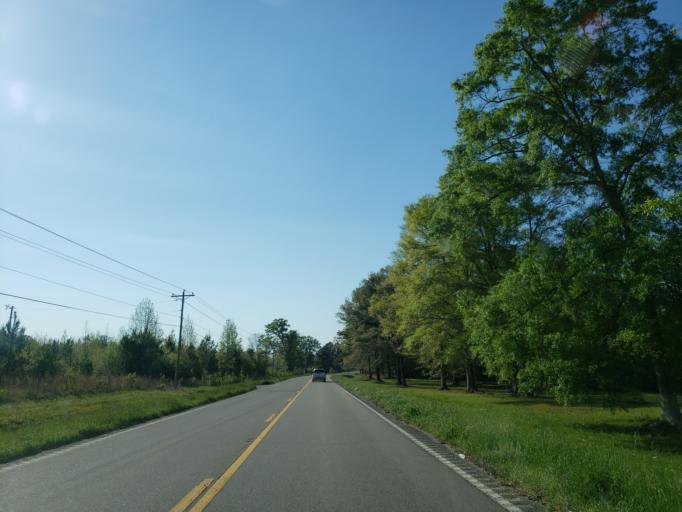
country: US
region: Mississippi
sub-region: Perry County
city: Richton
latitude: 31.4618
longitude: -88.9866
